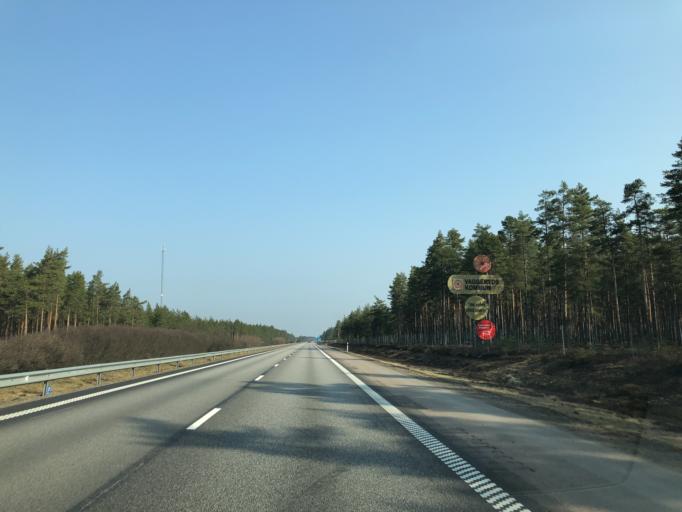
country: SE
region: Joenkoeping
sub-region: Vaggeryds Kommun
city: Skillingaryd
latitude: 57.3264
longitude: 14.1010
